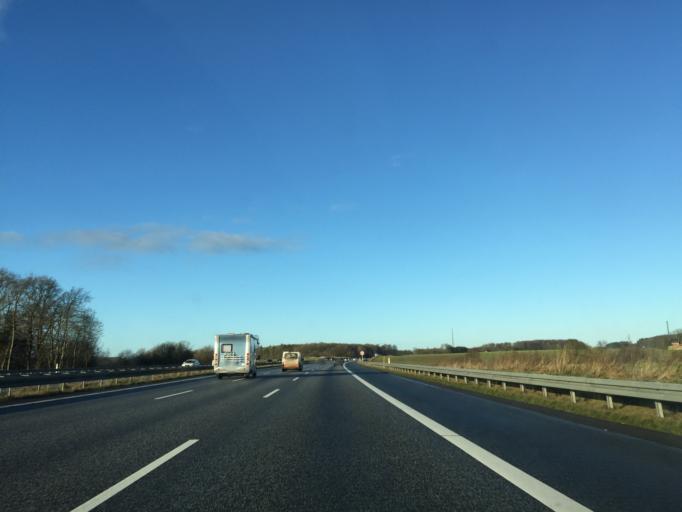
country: DK
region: South Denmark
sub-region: Vejle Kommune
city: Borkop
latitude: 55.6257
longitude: 9.5694
